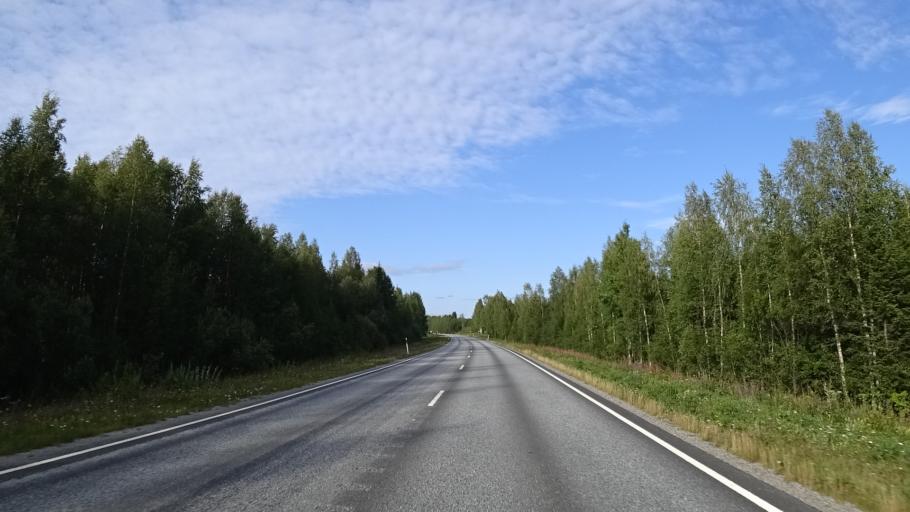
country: FI
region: North Karelia
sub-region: Joensuu
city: Eno
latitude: 62.8163
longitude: 30.1829
